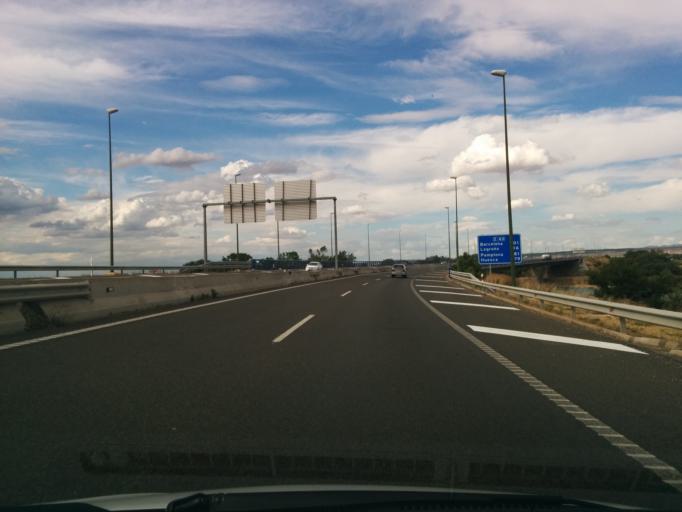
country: ES
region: Aragon
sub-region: Provincia de Zaragoza
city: Zaragoza
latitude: 41.6296
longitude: -0.8422
